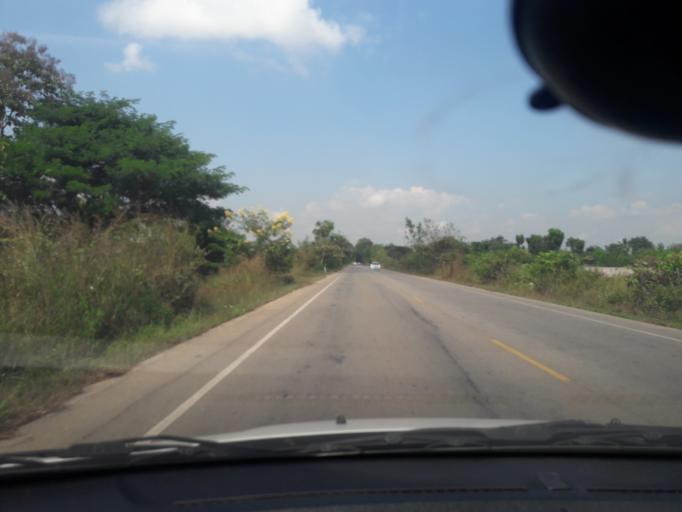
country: TH
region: Lampang
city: Mae Tha
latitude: 18.2072
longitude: 99.4984
